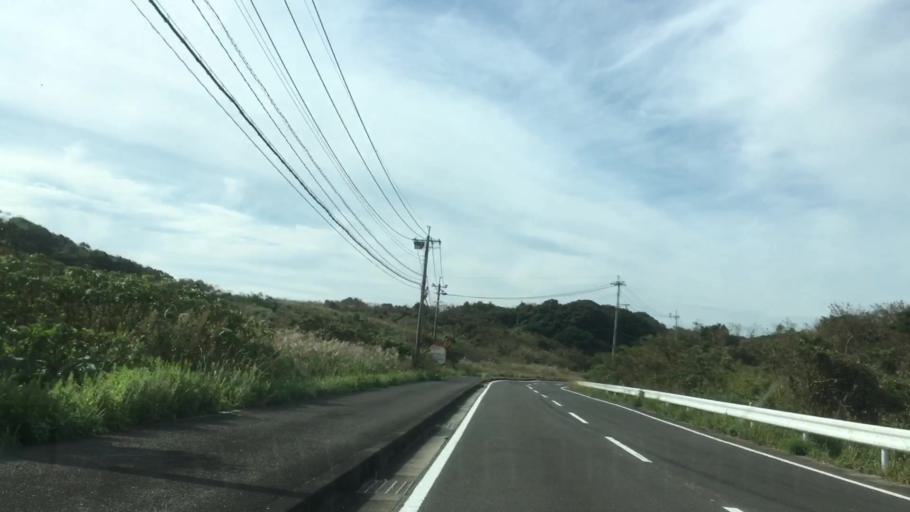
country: JP
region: Nagasaki
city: Sasebo
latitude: 33.0135
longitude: 129.5721
